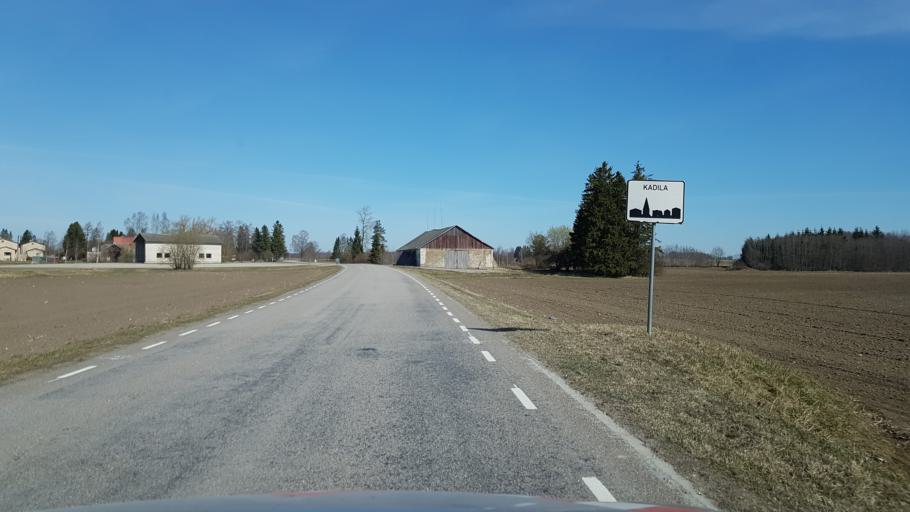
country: EE
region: Laeaene-Virumaa
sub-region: Vinni vald
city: Vinni
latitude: 59.2260
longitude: 26.3414
